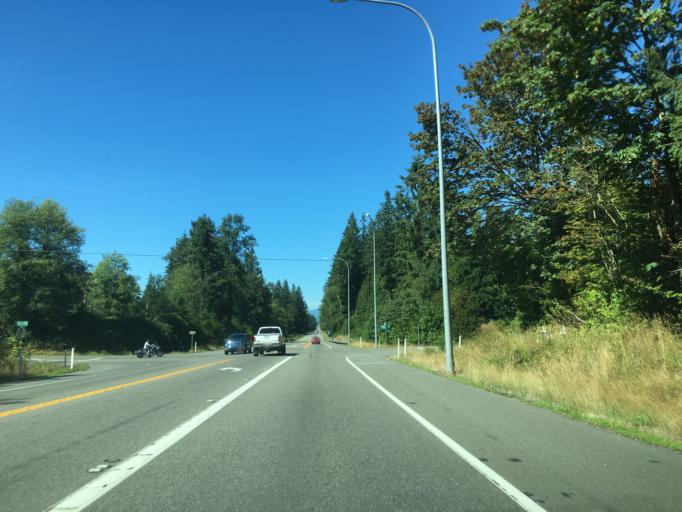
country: US
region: Washington
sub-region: Snohomish County
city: Sisco Heights
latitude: 48.0911
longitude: -122.1118
